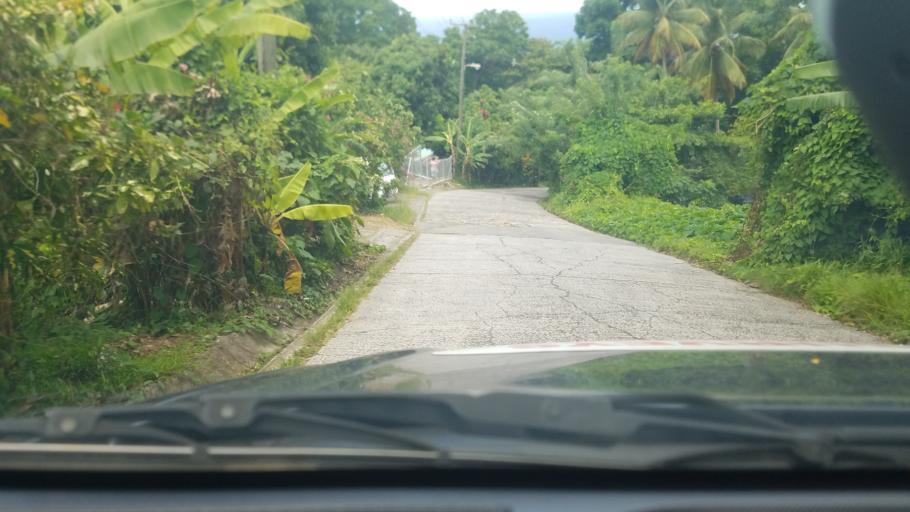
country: LC
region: Soufriere
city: Soufriere
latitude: 13.8427
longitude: -61.0603
